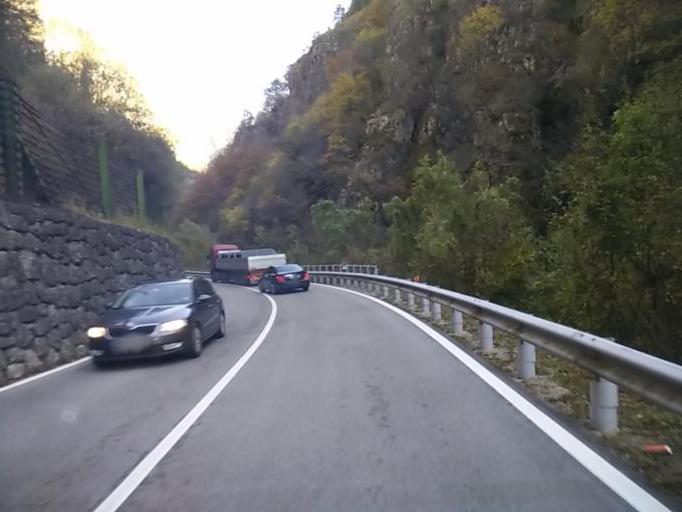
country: IT
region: Trentino-Alto Adige
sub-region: Provincia di Trento
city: Storo
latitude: 45.8452
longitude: 10.6047
